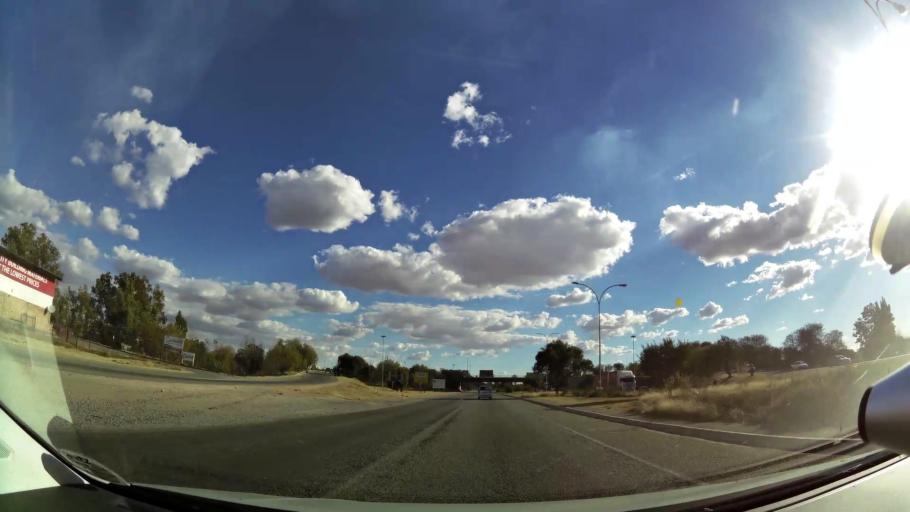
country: ZA
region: North-West
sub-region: Dr Kenneth Kaunda District Municipality
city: Klerksdorp
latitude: -26.8602
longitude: 26.6674
